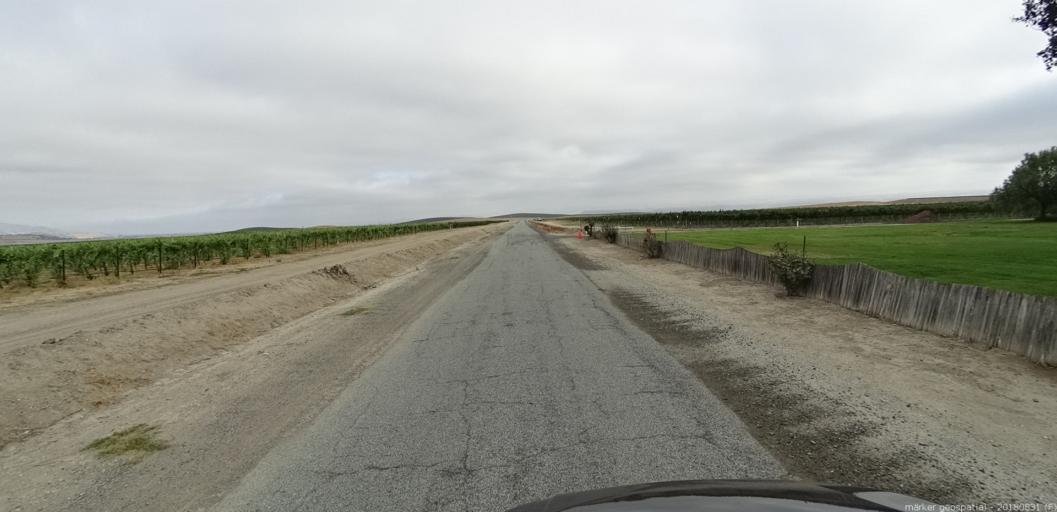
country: US
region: California
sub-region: Monterey County
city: King City
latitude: 36.1476
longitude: -121.1006
